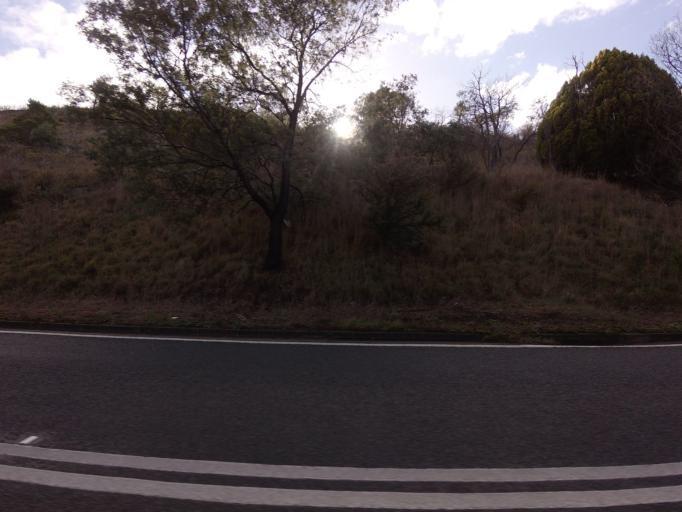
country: AU
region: Tasmania
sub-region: Derwent Valley
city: New Norfolk
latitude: -42.7271
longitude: 146.9553
